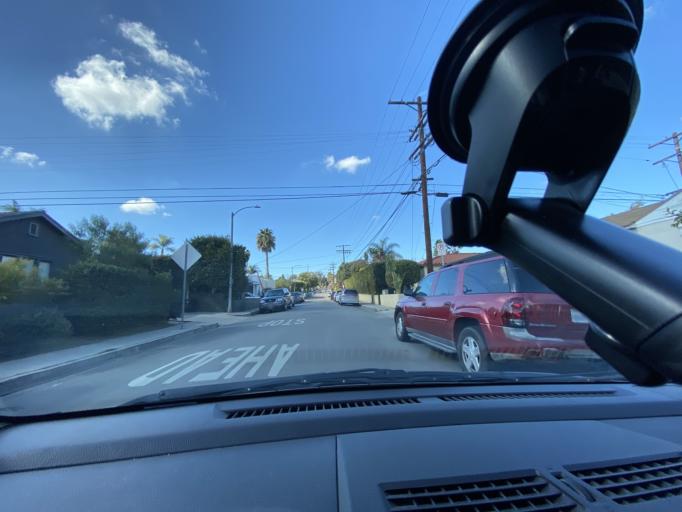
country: US
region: California
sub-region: Los Angeles County
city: Culver City
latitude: 34.0419
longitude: -118.3853
